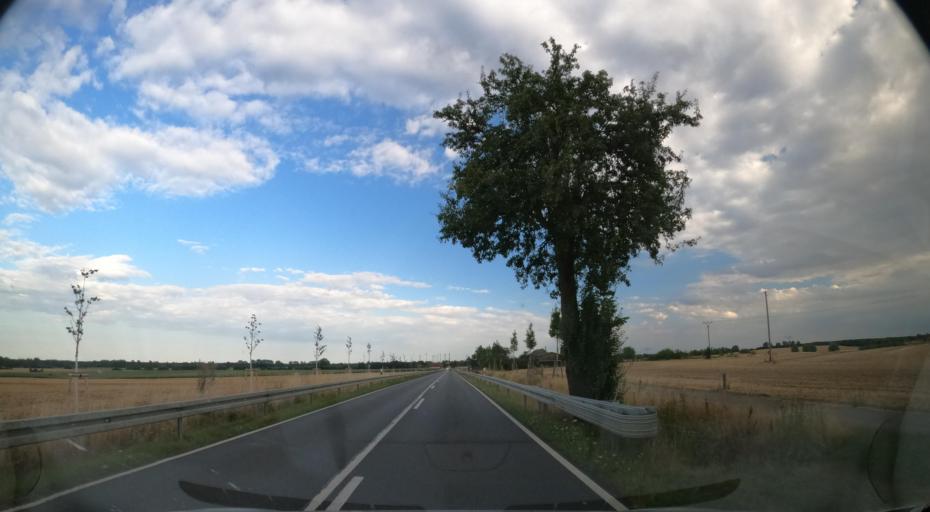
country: DE
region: Brandenburg
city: Brussow
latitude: 53.4828
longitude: 14.1094
